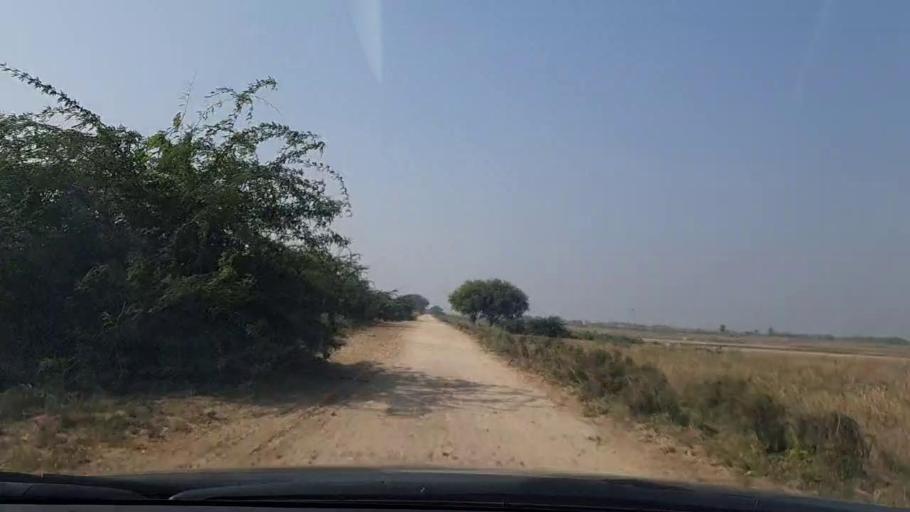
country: PK
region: Sindh
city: Mirpur Sakro
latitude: 24.5749
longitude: 67.7795
